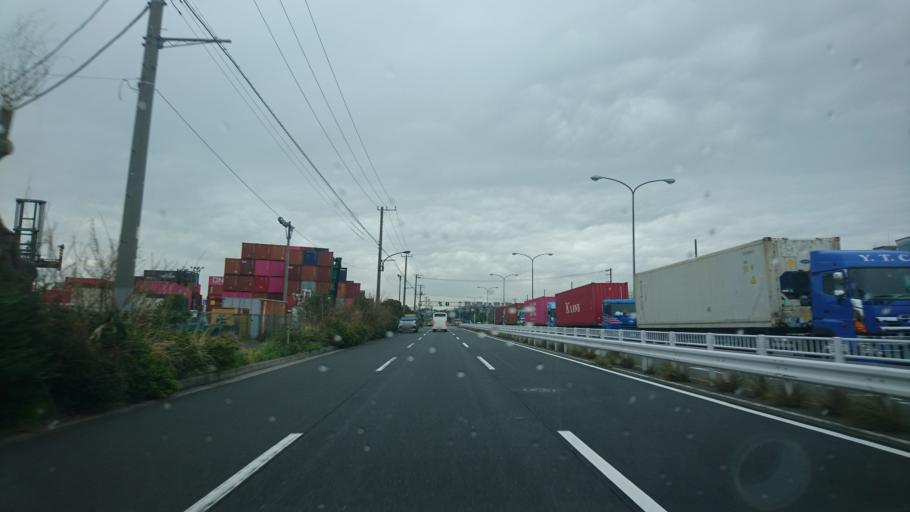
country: JP
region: Kanagawa
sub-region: Kawasaki-shi
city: Kawasaki
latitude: 35.6032
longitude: 139.7612
